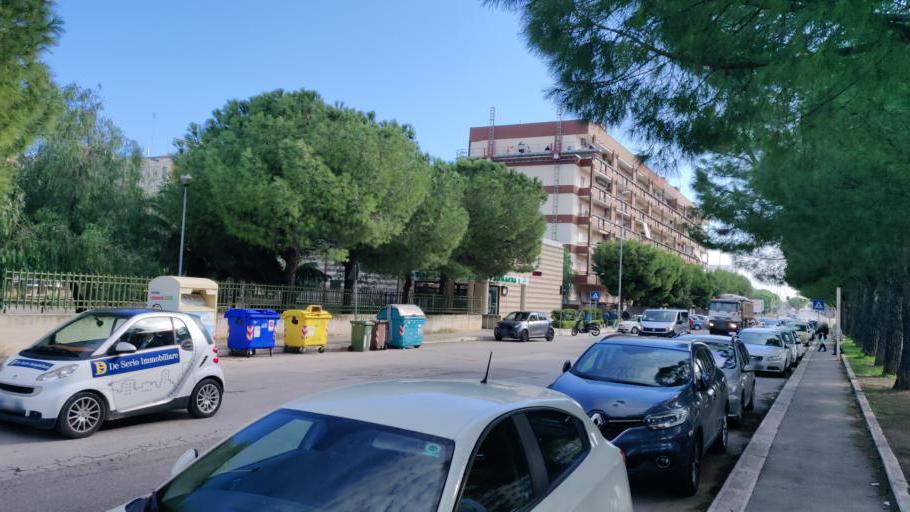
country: IT
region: Apulia
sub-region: Provincia di Bari
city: Bari
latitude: 41.1072
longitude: 16.8972
